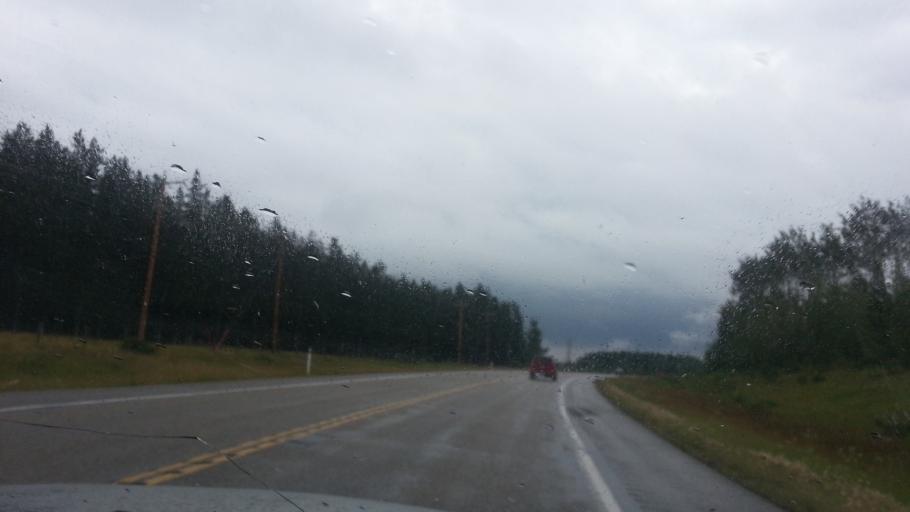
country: CA
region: Alberta
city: Cochrane
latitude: 50.9212
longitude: -114.6025
